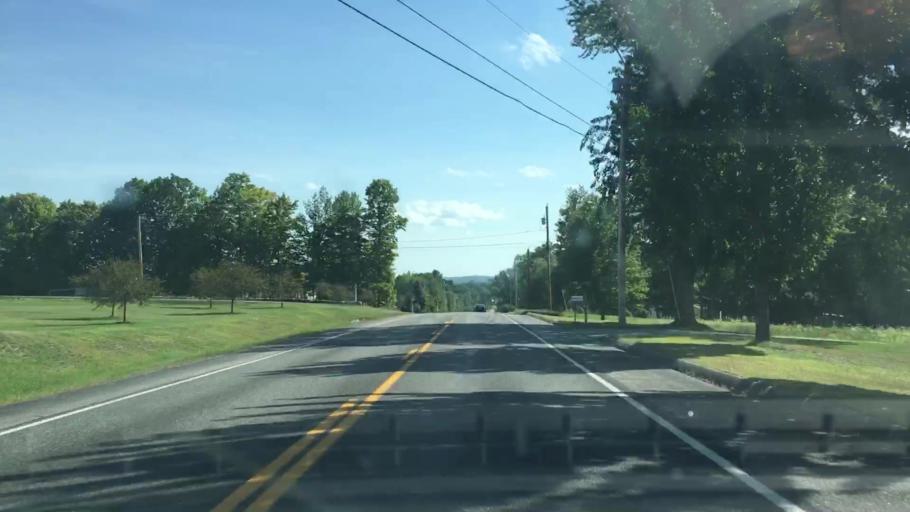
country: US
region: Maine
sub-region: Androscoggin County
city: Lisbon Falls
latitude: 44.0280
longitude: -70.0675
